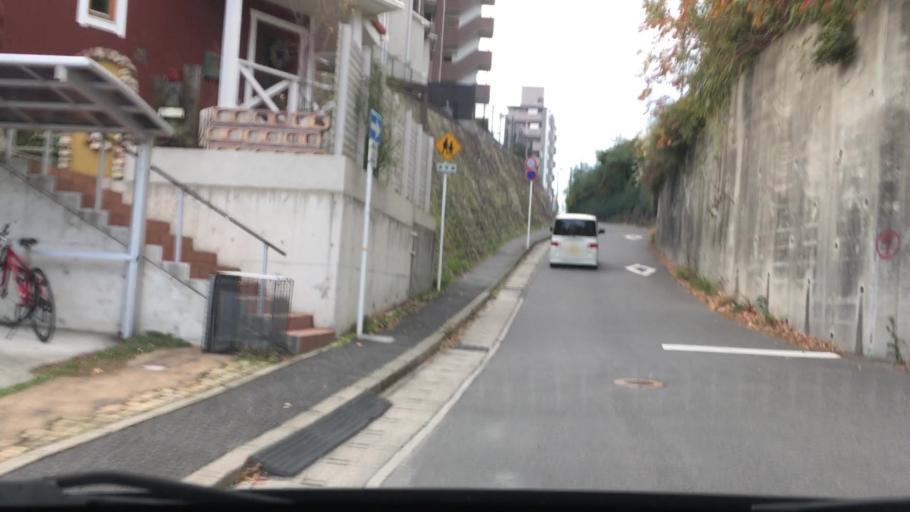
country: JP
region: Hiroshima
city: Hiroshima-shi
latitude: 34.3926
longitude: 132.4124
